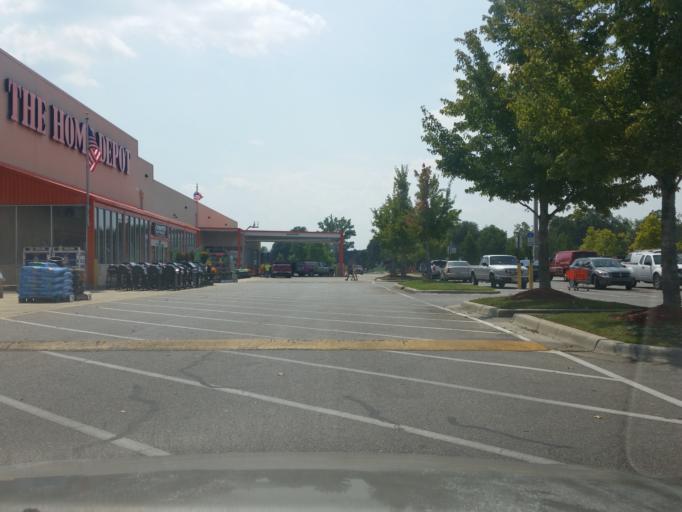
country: US
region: Florida
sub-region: Escambia County
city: Ensley
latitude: 30.5318
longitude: -87.2801
